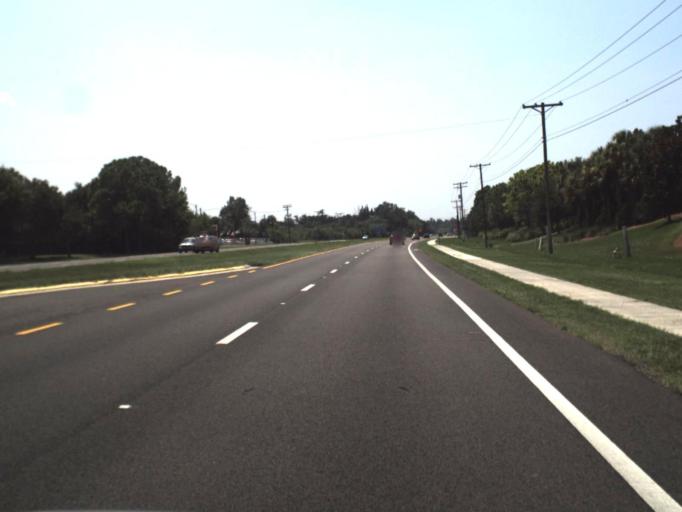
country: US
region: Florida
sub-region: Hillsborough County
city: Ruskin
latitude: 27.7444
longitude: -82.4188
